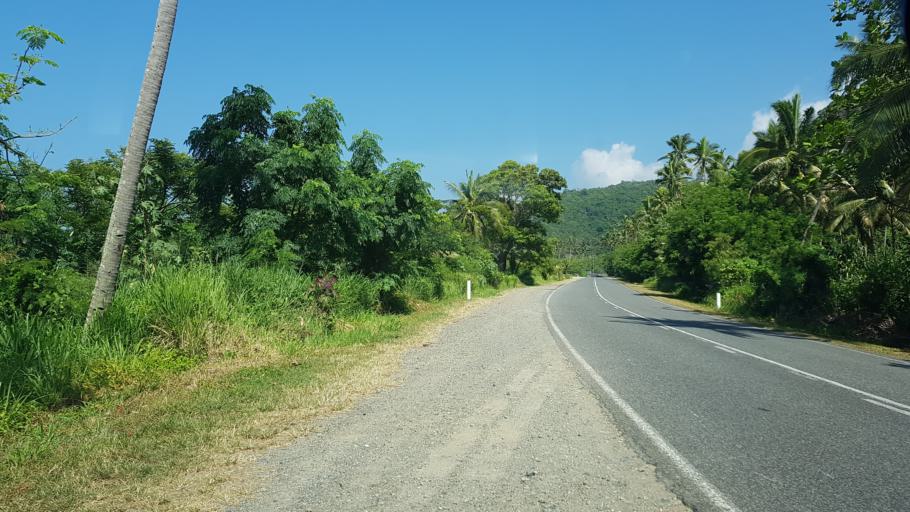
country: FJ
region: Western
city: Nadi
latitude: -18.1851
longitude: 177.6118
